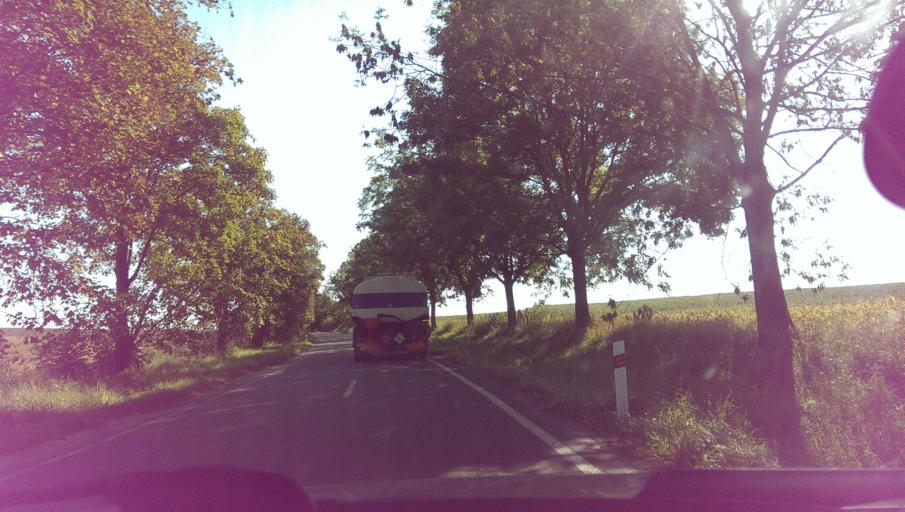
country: CZ
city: Brusperk
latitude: 49.6885
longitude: 18.2111
